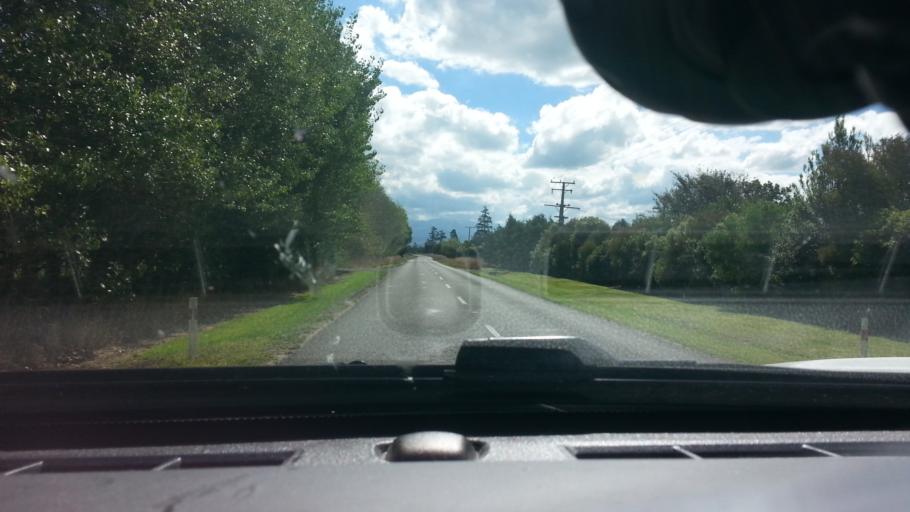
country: NZ
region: Wellington
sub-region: Masterton District
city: Masterton
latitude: -40.9544
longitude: 175.7080
